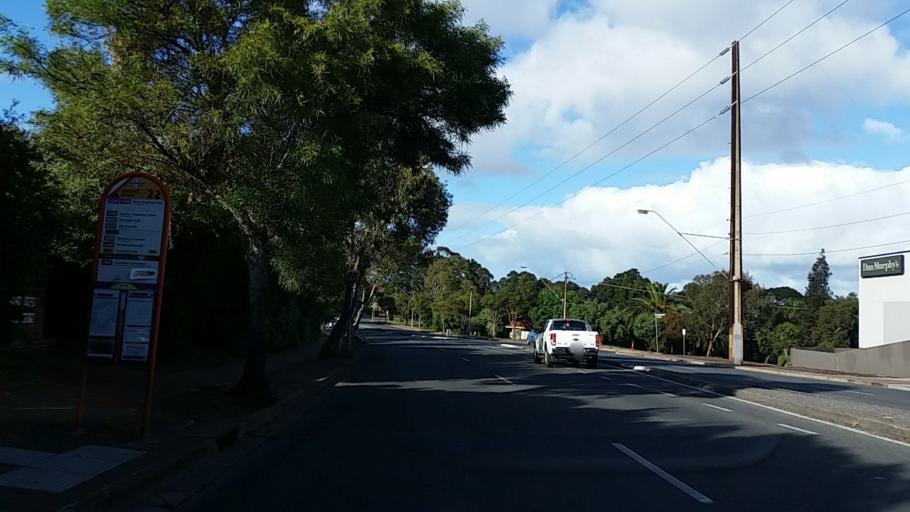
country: AU
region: South Australia
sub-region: Mitcham
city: Clapham
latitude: -35.0018
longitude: 138.5906
